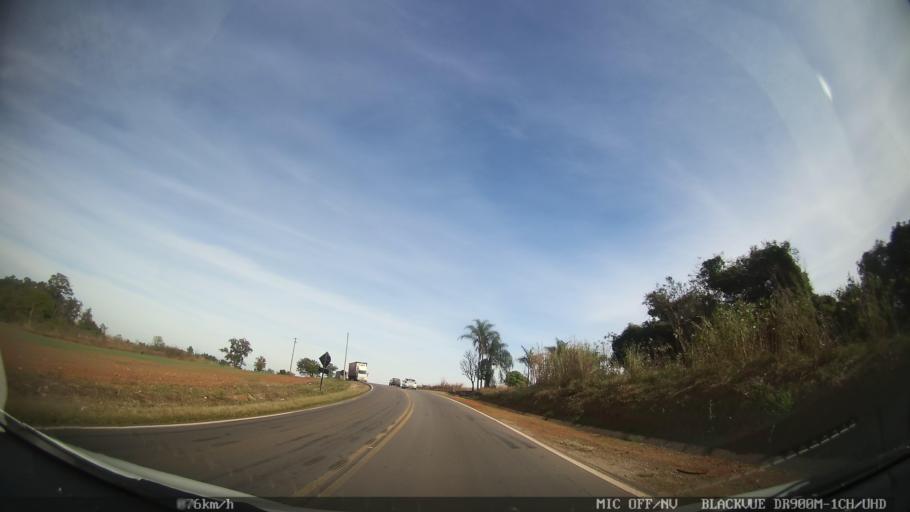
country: BR
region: Sao Paulo
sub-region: Rio Das Pedras
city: Rio das Pedras
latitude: -22.7888
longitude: -47.6345
